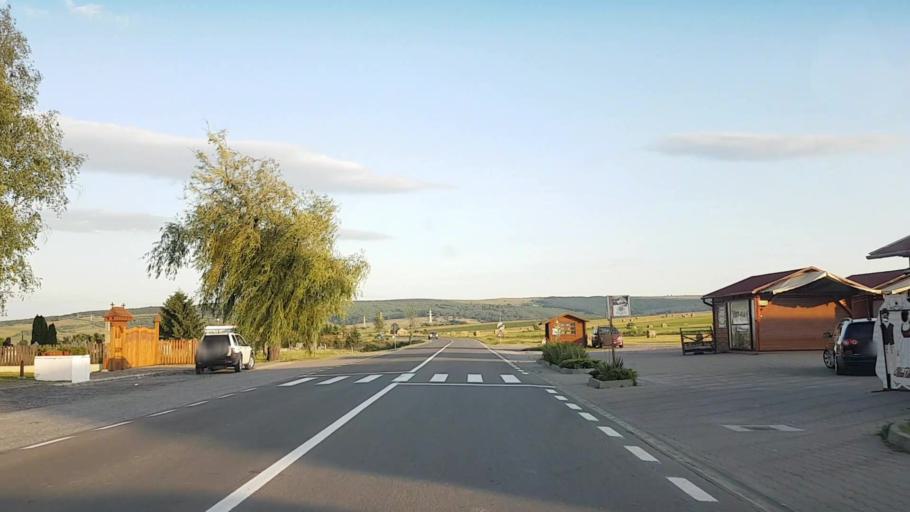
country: RO
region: Harghita
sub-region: Comuna Lupeni
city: Lupeni
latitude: 46.3763
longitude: 25.2197
